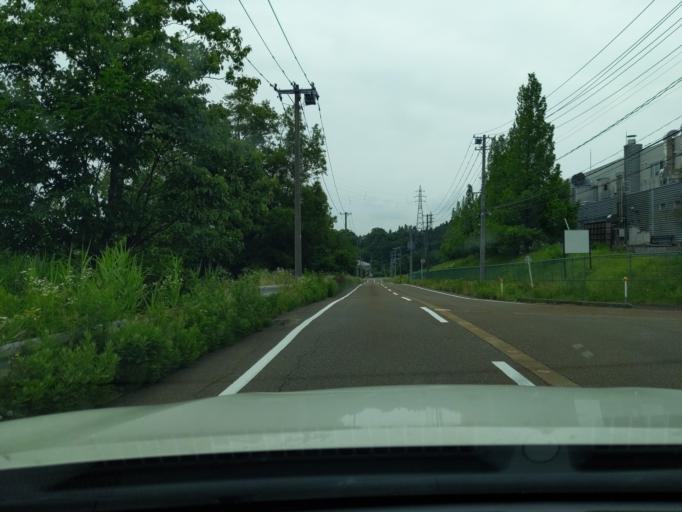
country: JP
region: Niigata
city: Kashiwazaki
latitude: 37.3458
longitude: 138.5981
